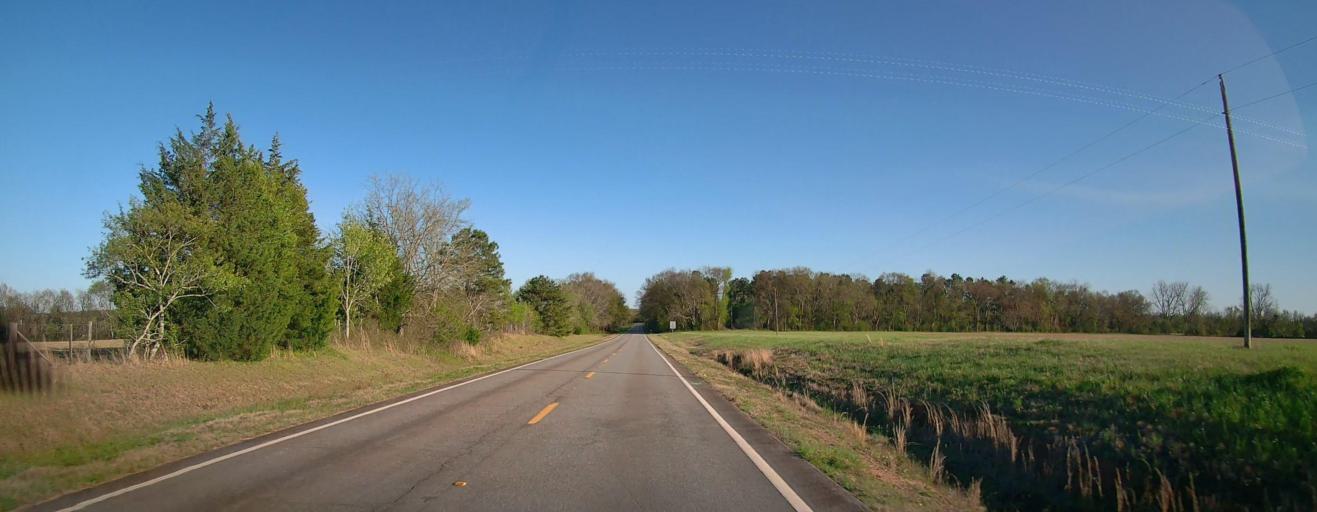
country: US
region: Georgia
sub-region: Baldwin County
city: Hardwick
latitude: 32.9625
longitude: -83.1713
